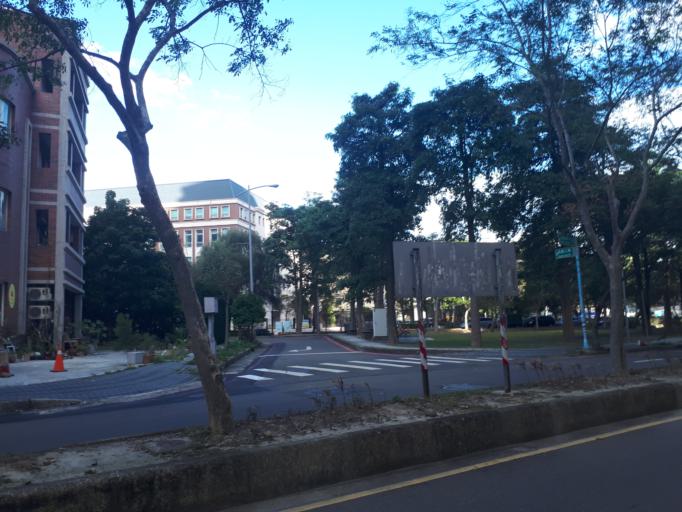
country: TW
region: Taiwan
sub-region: Hsinchu
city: Zhubei
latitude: 24.8023
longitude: 121.0369
